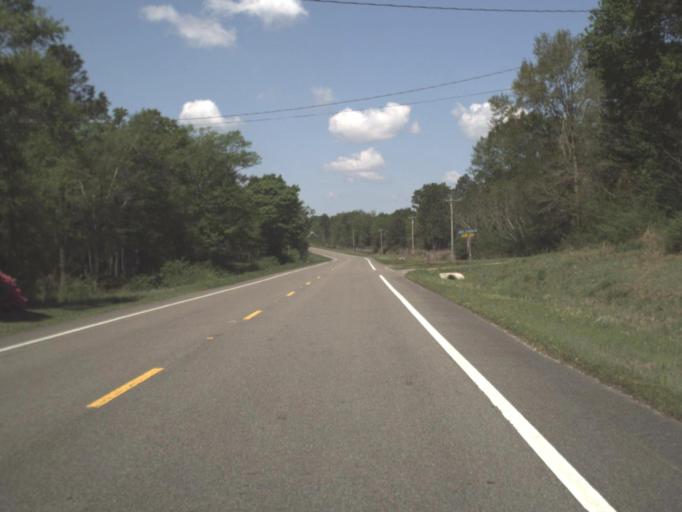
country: US
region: Alabama
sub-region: Escambia County
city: East Brewton
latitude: 30.8968
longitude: -86.9911
